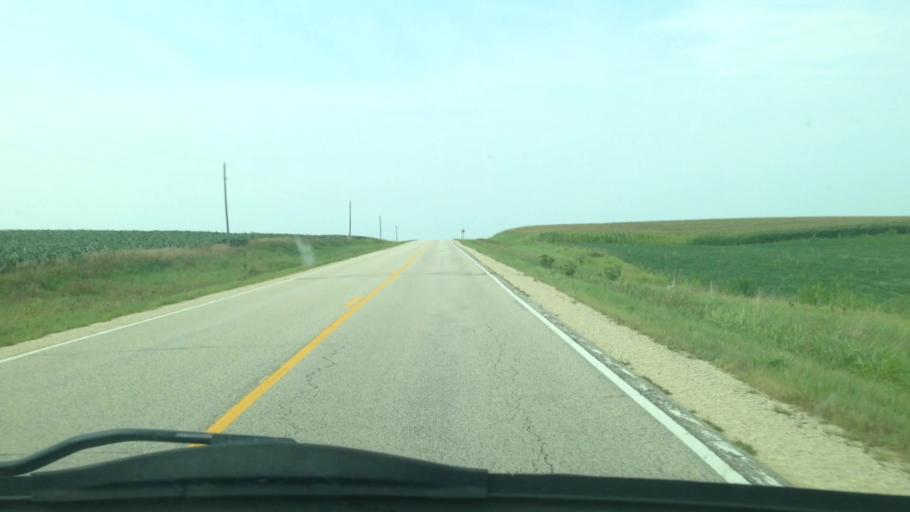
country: US
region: Minnesota
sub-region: Winona County
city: Saint Charles
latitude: 43.8580
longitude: -91.9593
